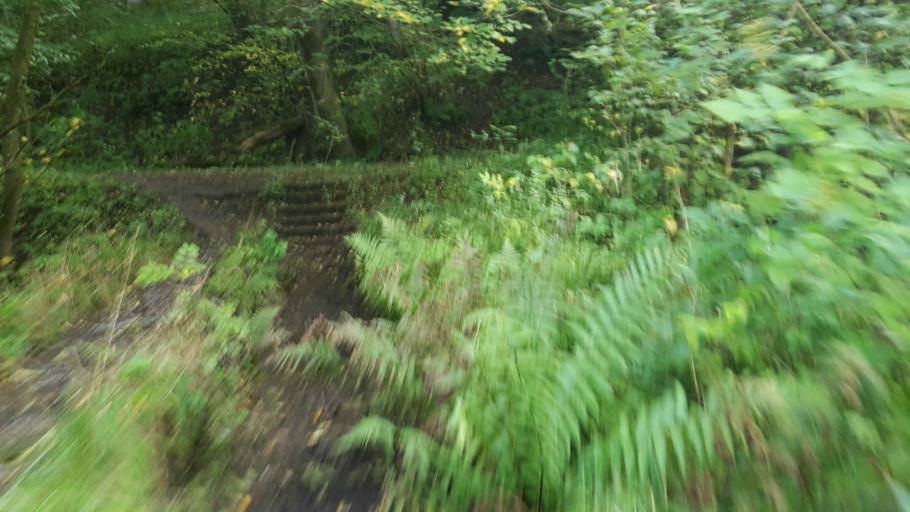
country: GB
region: Scotland
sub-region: South Lanarkshire
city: Law
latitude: 55.7297
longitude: -3.8619
